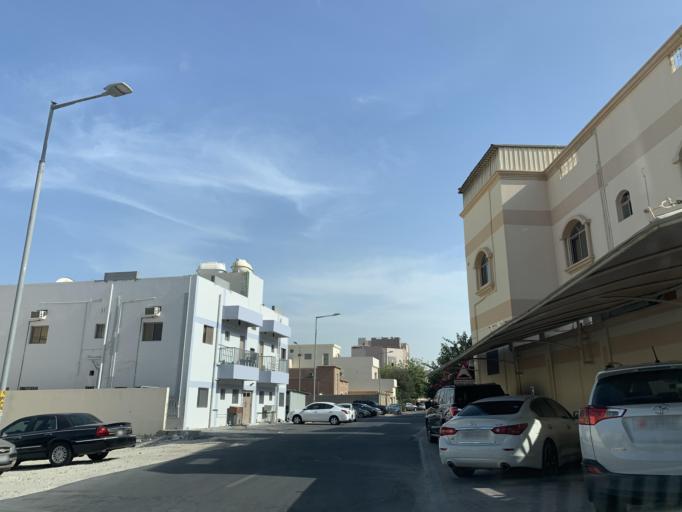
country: BH
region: Northern
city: Ar Rifa'
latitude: 26.1282
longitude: 50.5805
